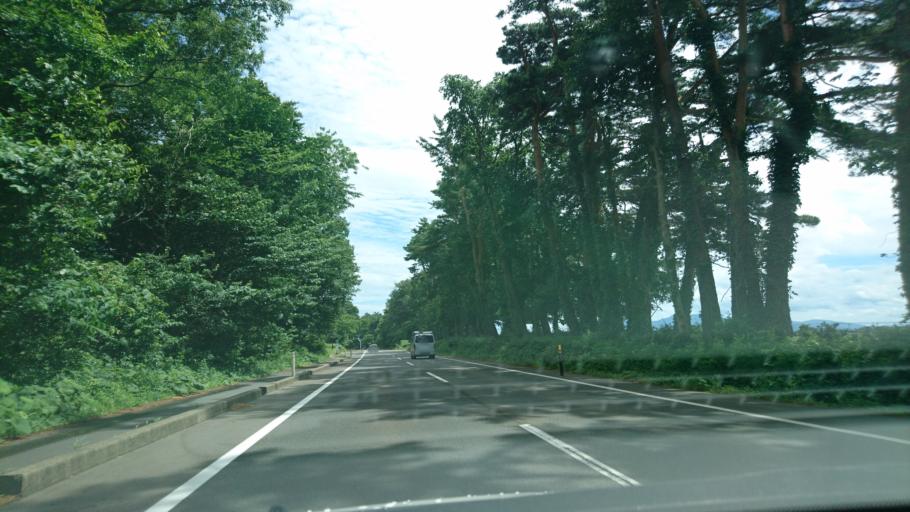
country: JP
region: Iwate
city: Morioka-shi
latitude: 39.7788
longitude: 141.1262
